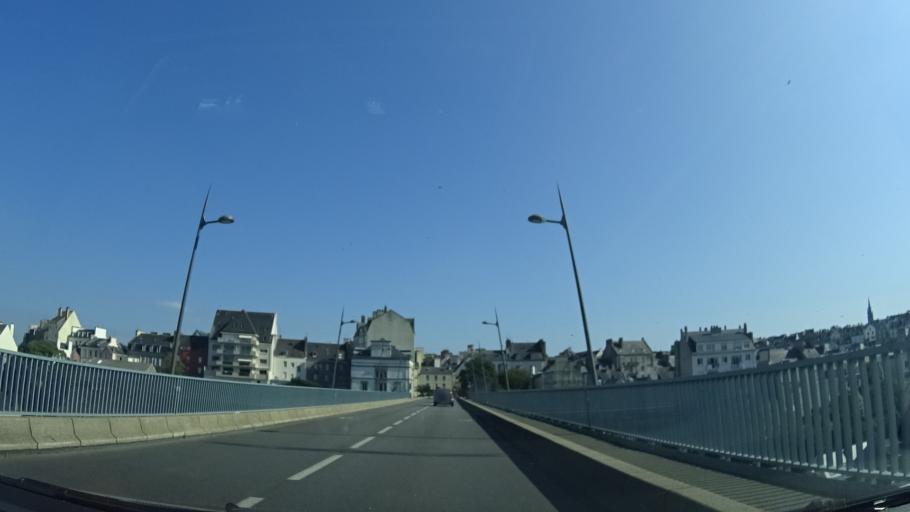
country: FR
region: Brittany
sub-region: Departement du Finistere
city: Douarnenez
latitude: 48.0899
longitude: -4.3332
